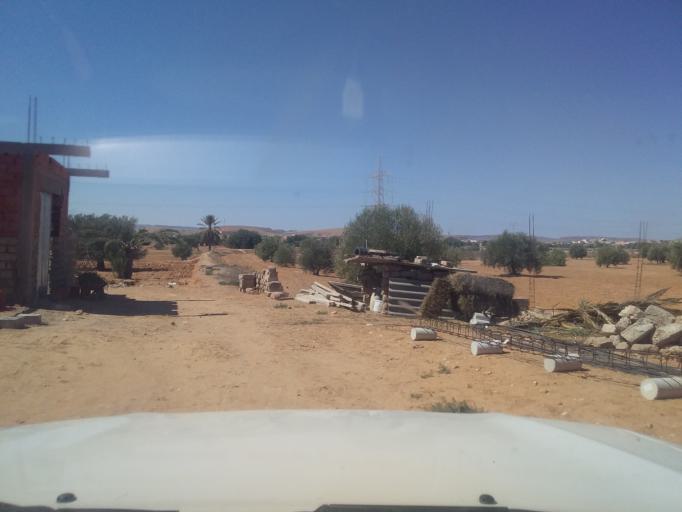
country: TN
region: Qabis
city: Matmata
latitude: 33.5806
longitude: 10.2804
